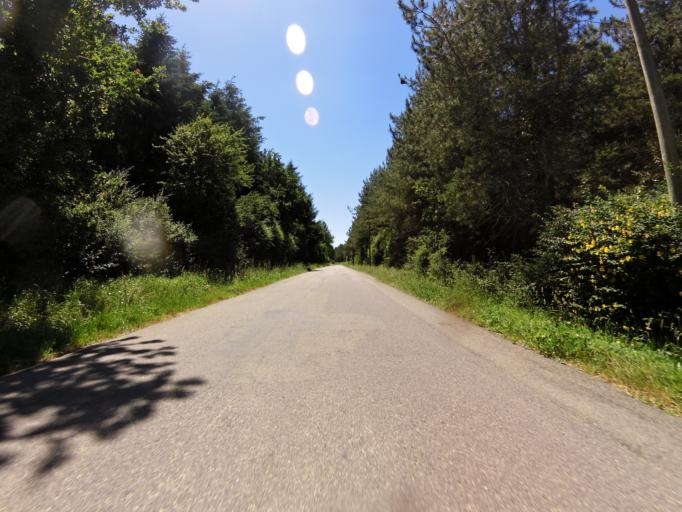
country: FR
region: Brittany
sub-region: Departement du Morbihan
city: Penestin
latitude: 47.4756
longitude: -2.4527
